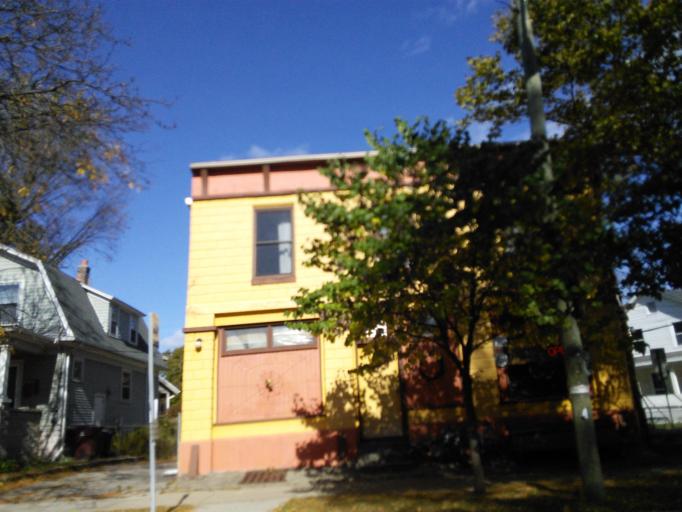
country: US
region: Michigan
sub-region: Washtenaw County
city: Ann Arbor
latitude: 42.2839
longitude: -83.7527
